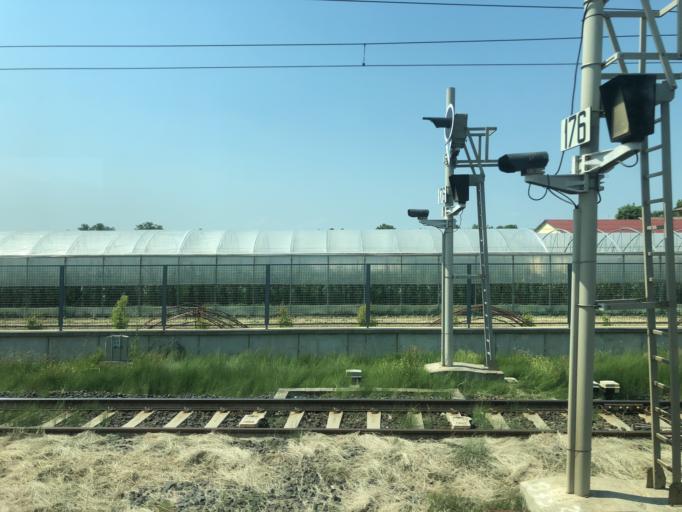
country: IT
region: Emilia-Romagna
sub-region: Forli-Cesena
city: Forlimpopoli
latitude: 44.2024
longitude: 12.1084
